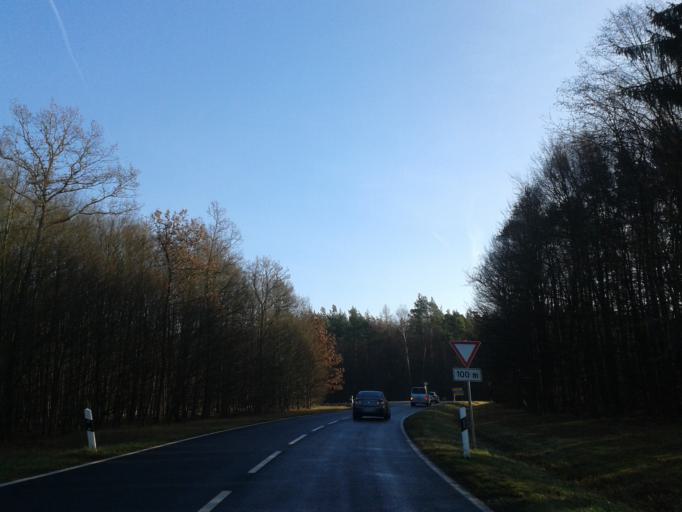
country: DE
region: Bavaria
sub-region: Regierungsbezirk Unterfranken
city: Aidhausen
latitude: 50.1048
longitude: 10.4123
